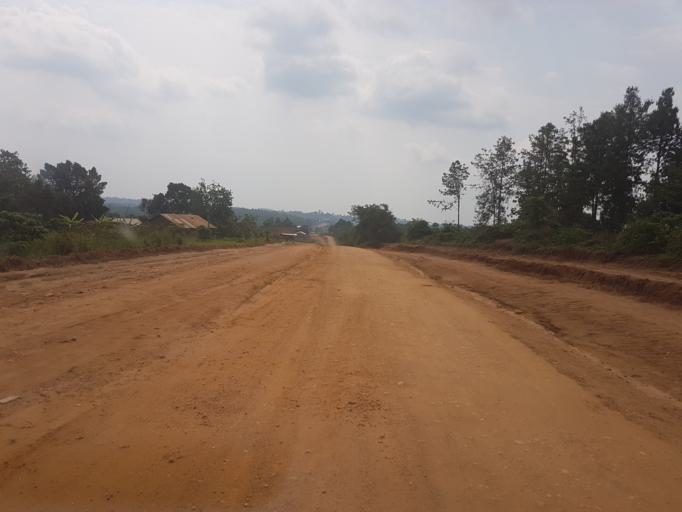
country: UG
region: Western Region
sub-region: Kanungu District
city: Ntungamo
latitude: -0.8098
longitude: 29.7057
